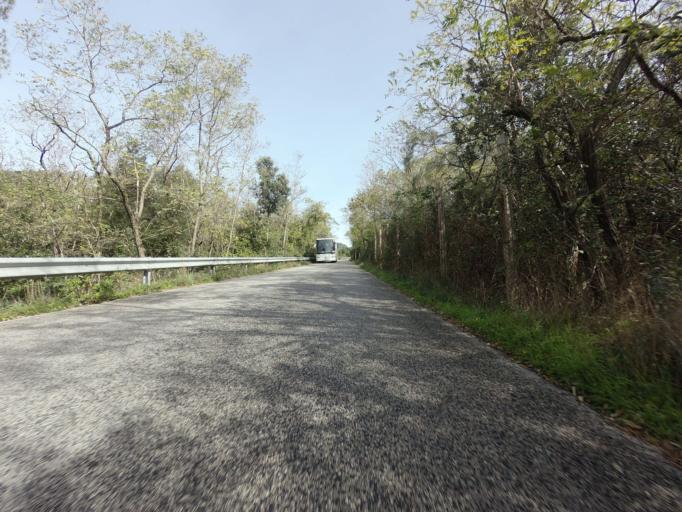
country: IT
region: Campania
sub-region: Provincia di Napoli
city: Pollena Trocchia
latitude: 40.8294
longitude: 14.4197
